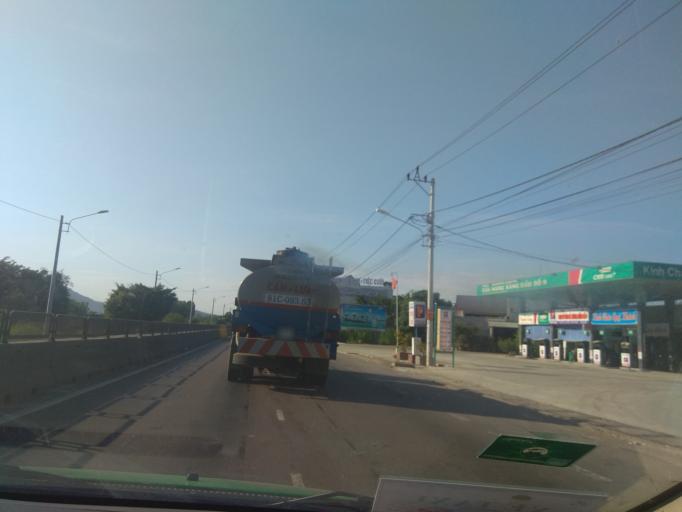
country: VN
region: Binh Dinh
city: Tuy Phuoc
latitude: 13.8237
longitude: 109.1453
